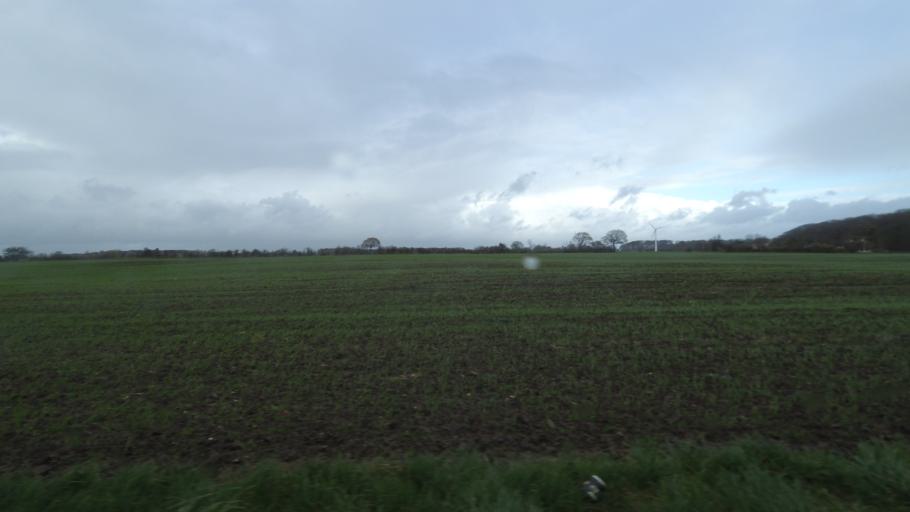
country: DK
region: Central Jutland
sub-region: Odder Kommune
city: Odder
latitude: 55.9185
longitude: 10.2205
